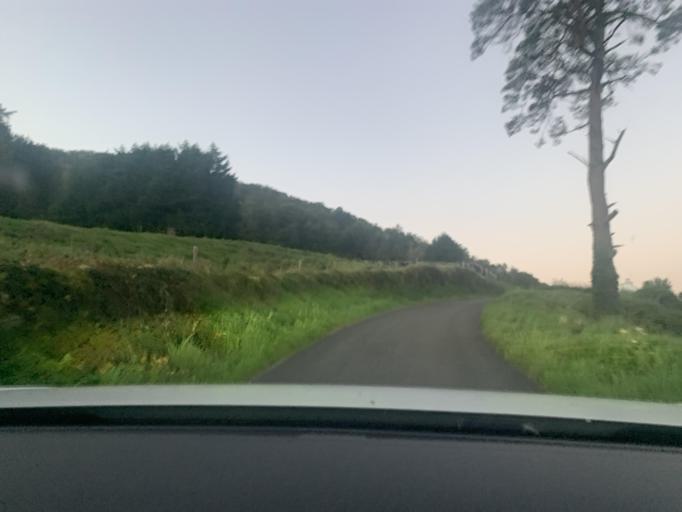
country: IE
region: Connaught
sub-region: County Leitrim
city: Manorhamilton
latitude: 54.2627
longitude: -8.2954
